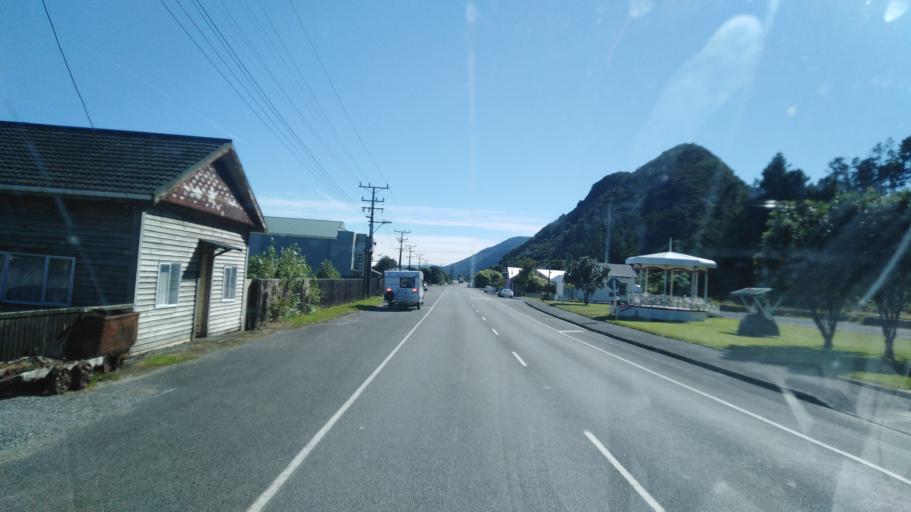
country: NZ
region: West Coast
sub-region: Buller District
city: Westport
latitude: -41.6295
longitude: 171.8541
